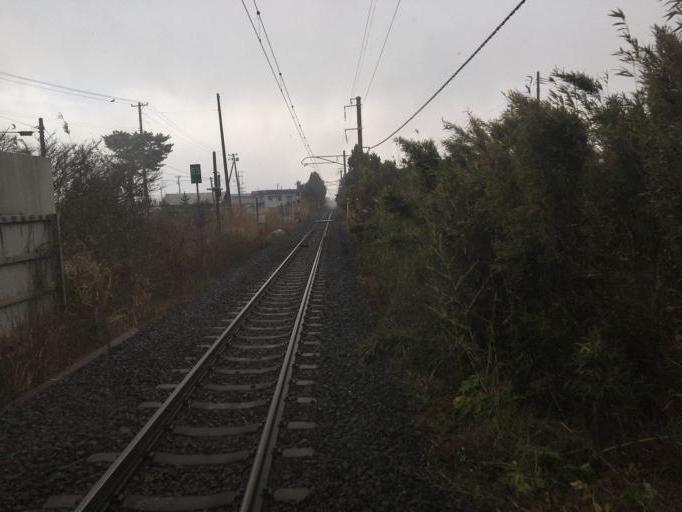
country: JP
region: Aomori
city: Aomori Shi
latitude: 40.9821
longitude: 140.6539
